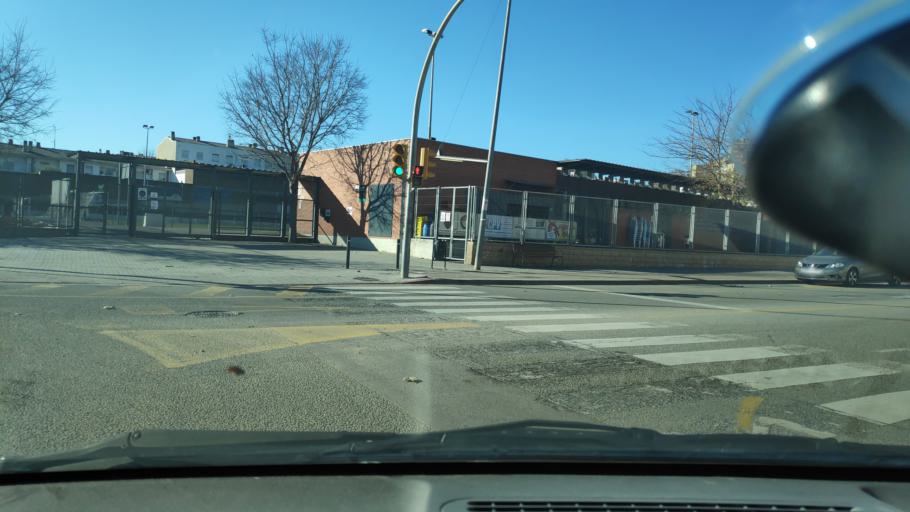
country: ES
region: Catalonia
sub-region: Provincia de Barcelona
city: Sant Quirze del Valles
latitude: 41.5413
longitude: 2.0922
